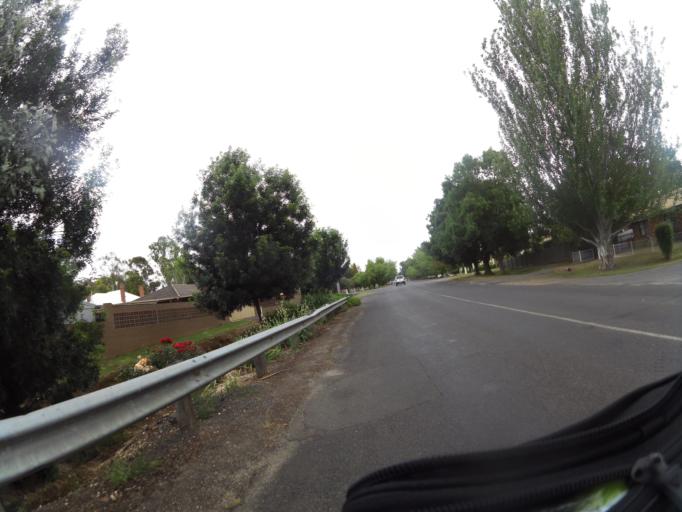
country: AU
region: Victoria
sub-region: Mount Alexander
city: Castlemaine
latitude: -37.0688
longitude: 144.2120
